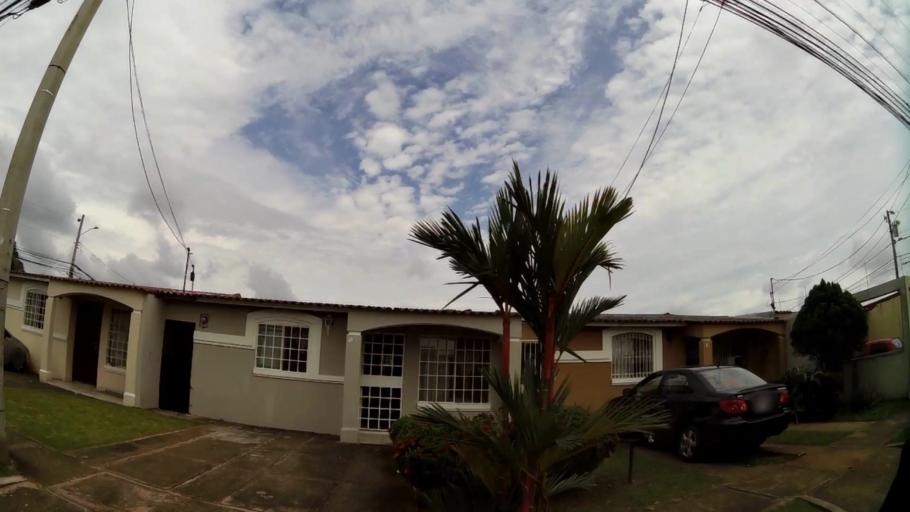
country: PA
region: Panama
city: Tocumen
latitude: 9.0408
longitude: -79.4085
